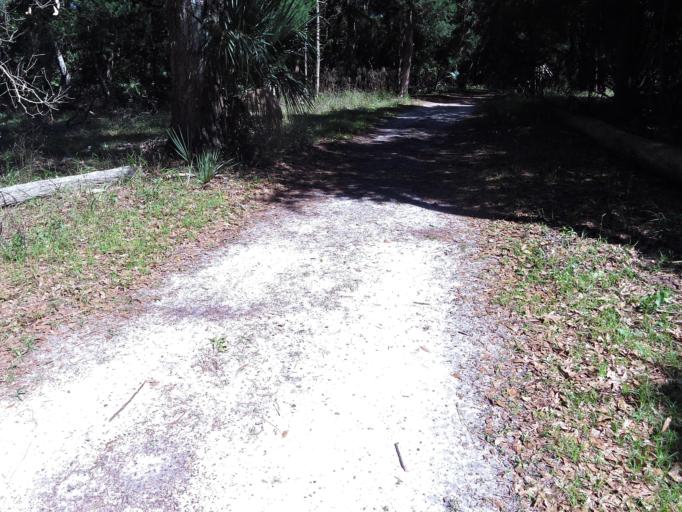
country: US
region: Florida
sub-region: Saint Johns County
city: Villano Beach
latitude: 30.0115
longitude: -81.3308
